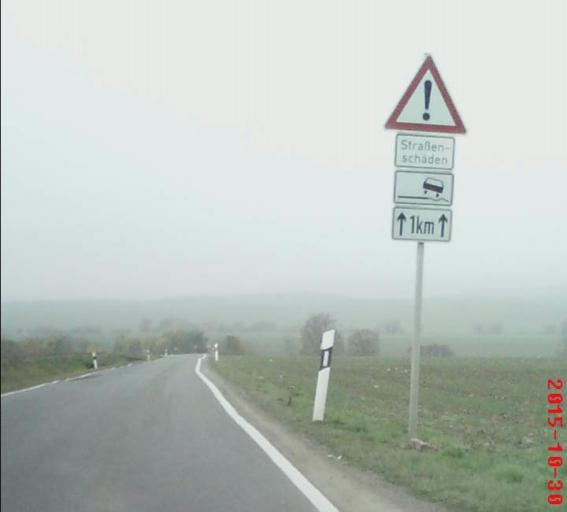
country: DE
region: Thuringia
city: Anrode
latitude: 51.2379
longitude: 10.3815
